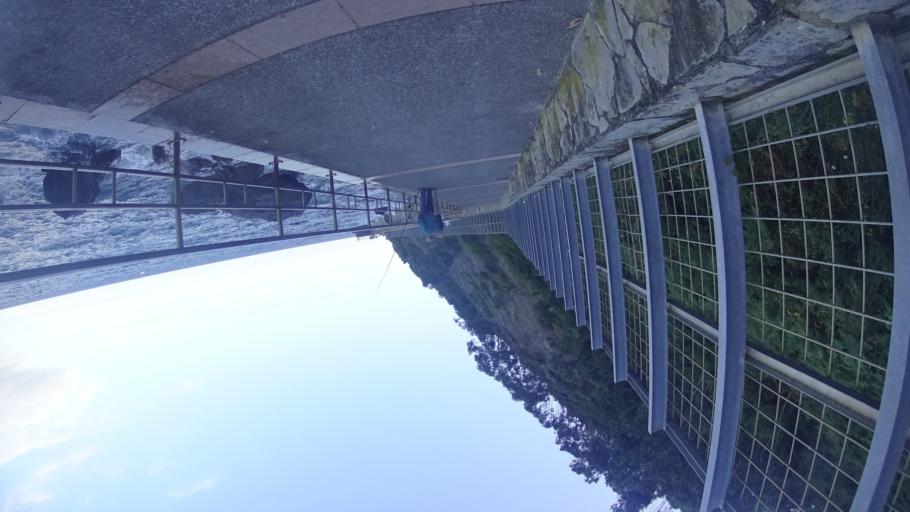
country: ES
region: Asturias
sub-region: Province of Asturias
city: Ribadesella
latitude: 43.4690
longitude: -5.0757
